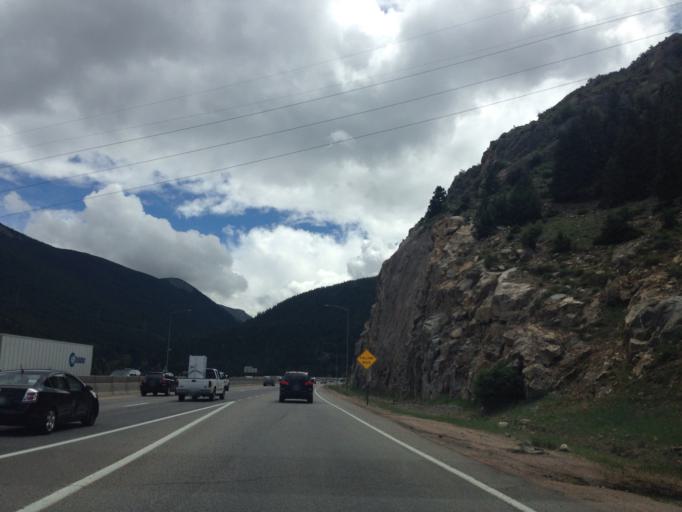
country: US
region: Colorado
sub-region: Clear Creek County
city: Georgetown
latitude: 39.7133
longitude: -105.6972
